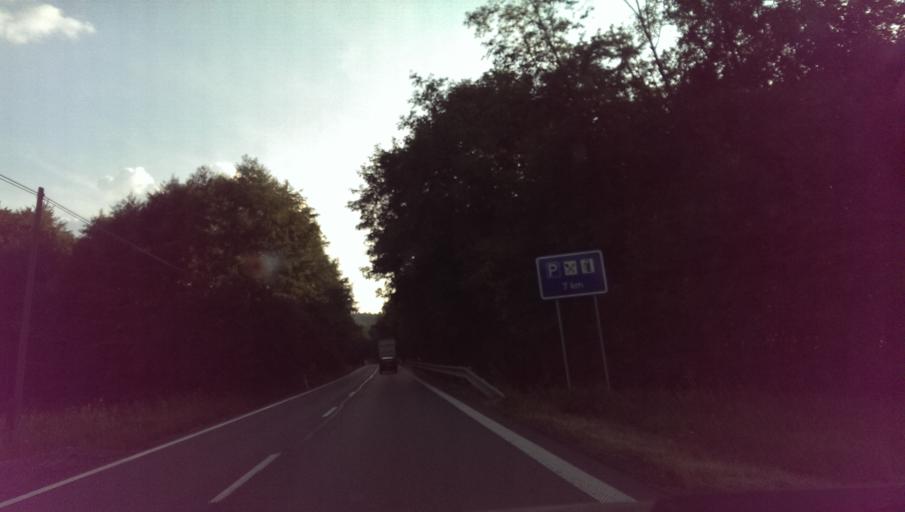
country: CZ
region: Zlin
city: Slusovice
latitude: 49.2079
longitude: 17.8080
